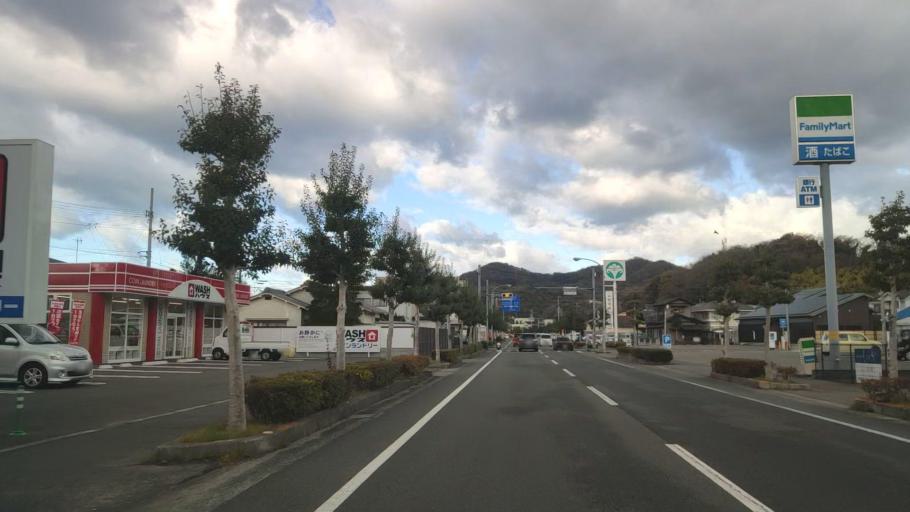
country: JP
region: Ehime
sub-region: Shikoku-chuo Shi
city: Matsuyama
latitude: 33.8696
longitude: 132.7228
